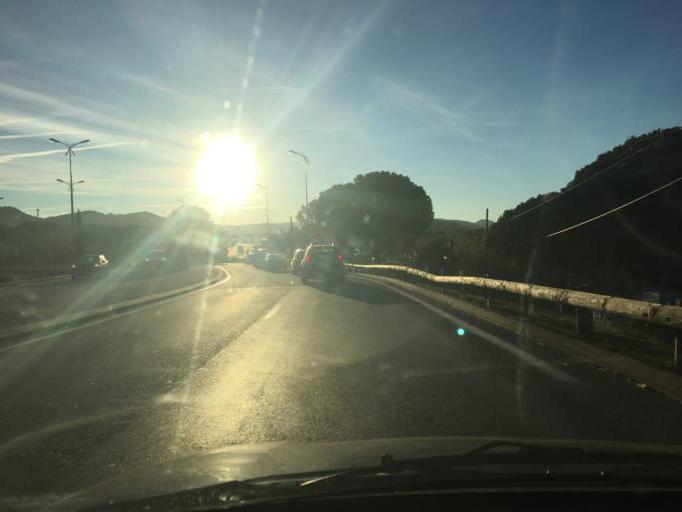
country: FR
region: Provence-Alpes-Cote d'Azur
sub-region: Departement du Var
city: Le Muy
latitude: 43.4634
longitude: 6.5470
